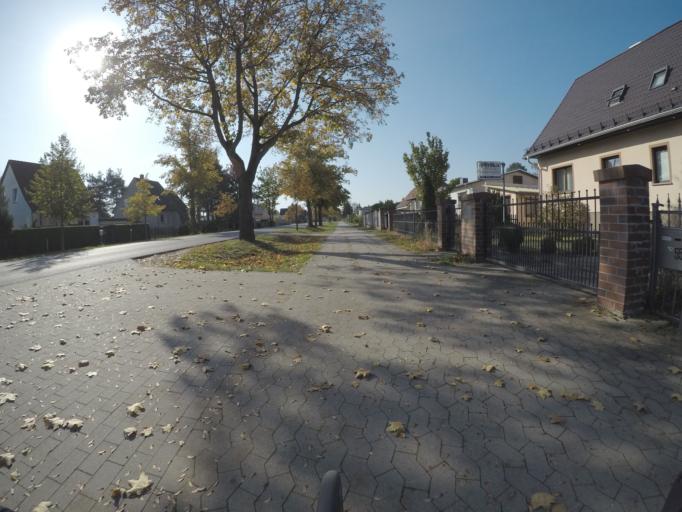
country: DE
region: Brandenburg
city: Oranienburg
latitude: 52.7364
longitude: 13.2471
